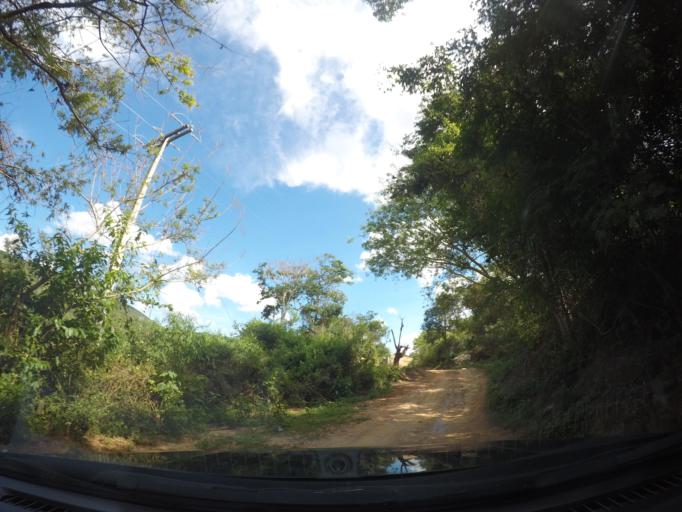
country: BR
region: Bahia
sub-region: Barra Da Estiva
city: Barra da Estiva
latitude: -13.1571
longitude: -41.5938
